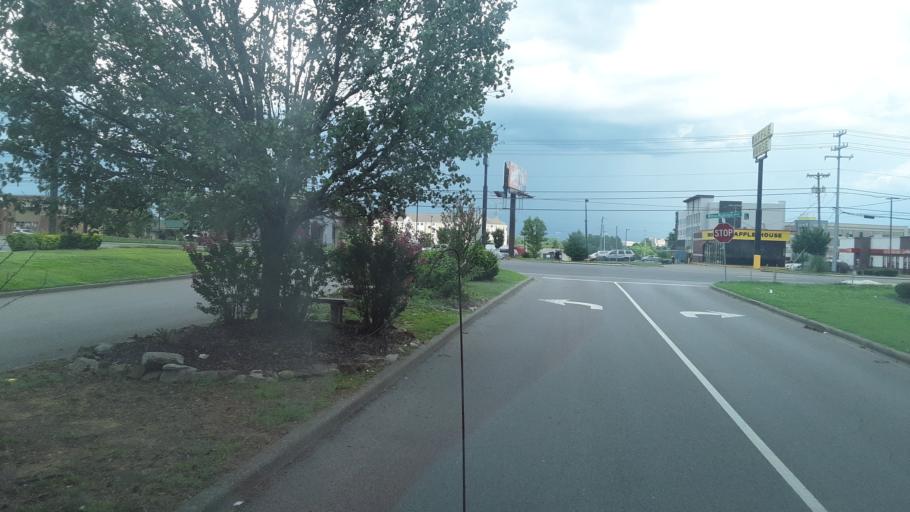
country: US
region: Tennessee
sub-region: Montgomery County
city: Clarksville
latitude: 36.5953
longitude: -87.2882
